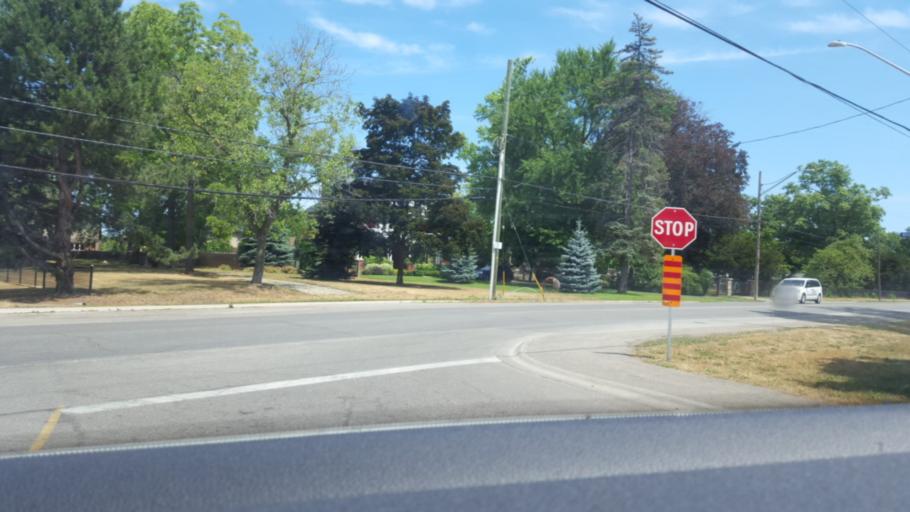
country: CA
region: Ontario
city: Hamilton
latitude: 43.1942
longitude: -79.5917
